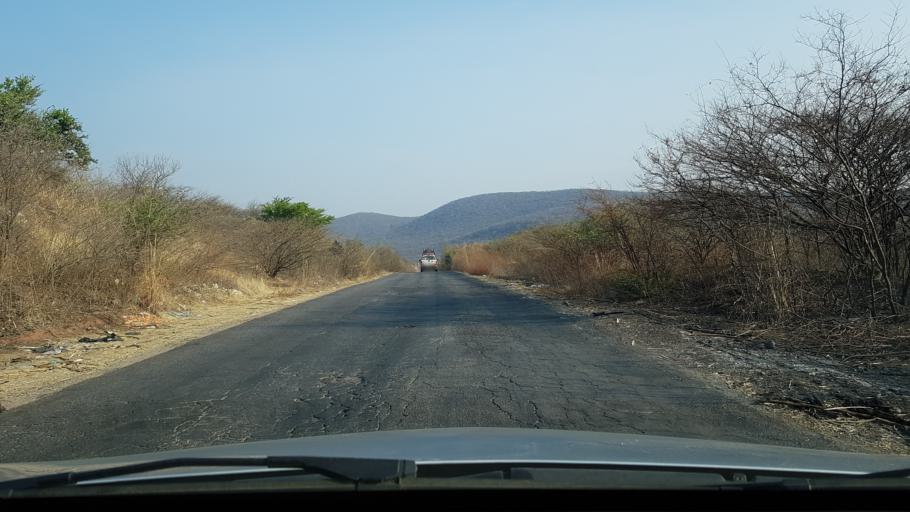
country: MX
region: Morelos
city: Tlaltizapan
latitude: 18.6651
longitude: -99.0519
